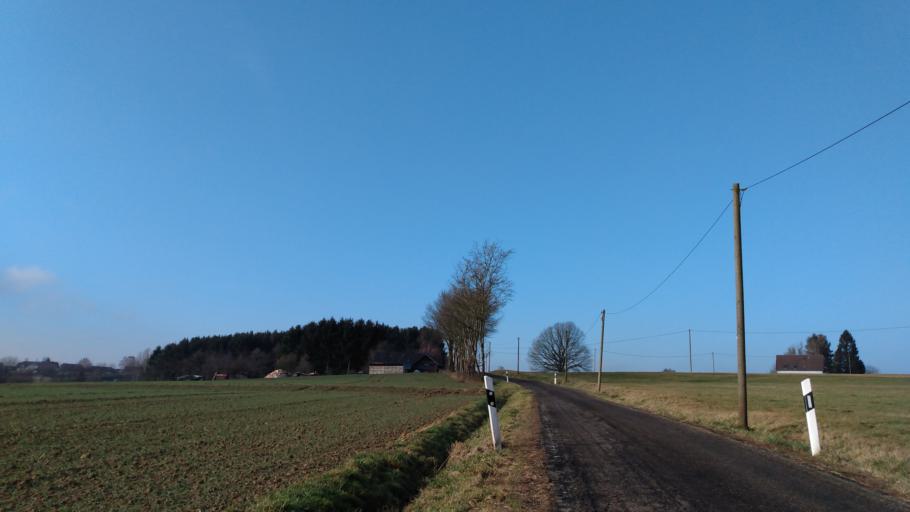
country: DE
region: Rheinland-Pfalz
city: Kircheib
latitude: 50.6853
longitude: 7.4589
